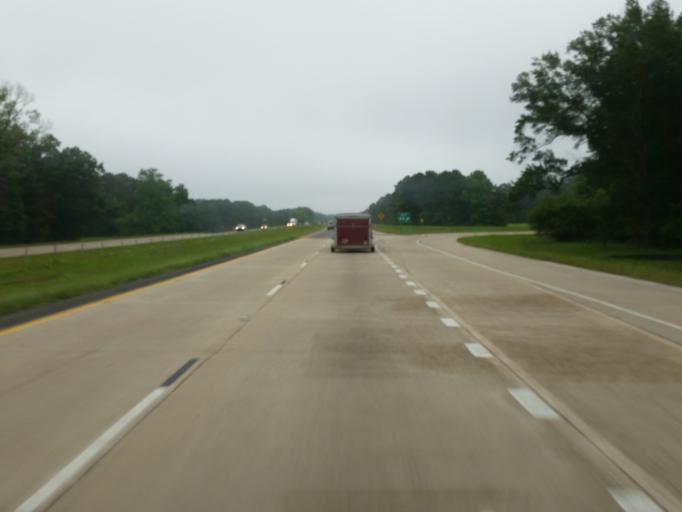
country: US
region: Louisiana
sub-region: Webster Parish
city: Minden
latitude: 32.5891
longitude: -93.3405
